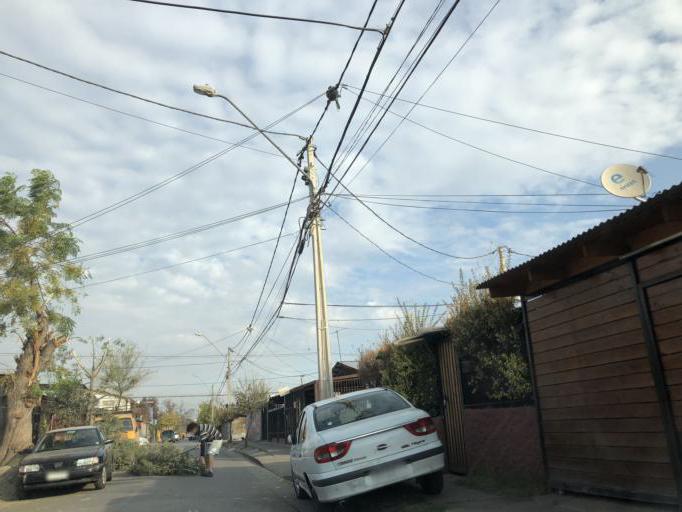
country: CL
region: Santiago Metropolitan
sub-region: Provincia de Cordillera
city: Puente Alto
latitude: -33.6020
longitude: -70.5618
